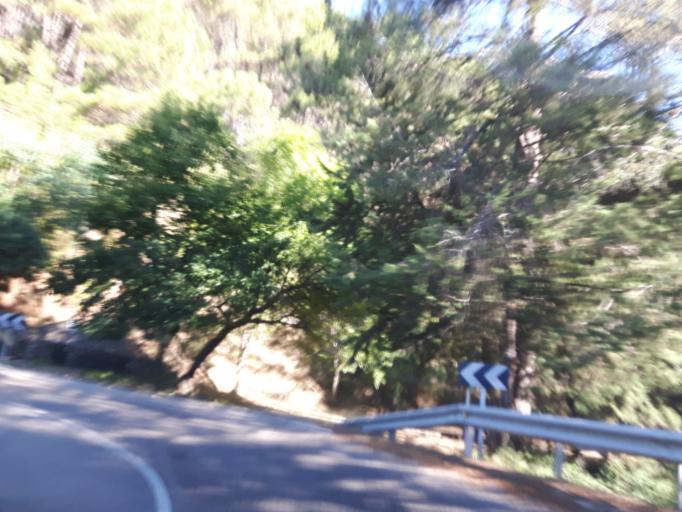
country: ES
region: Castille and Leon
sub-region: Provincia de Avila
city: Mombeltran
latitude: 40.2340
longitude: -5.0402
